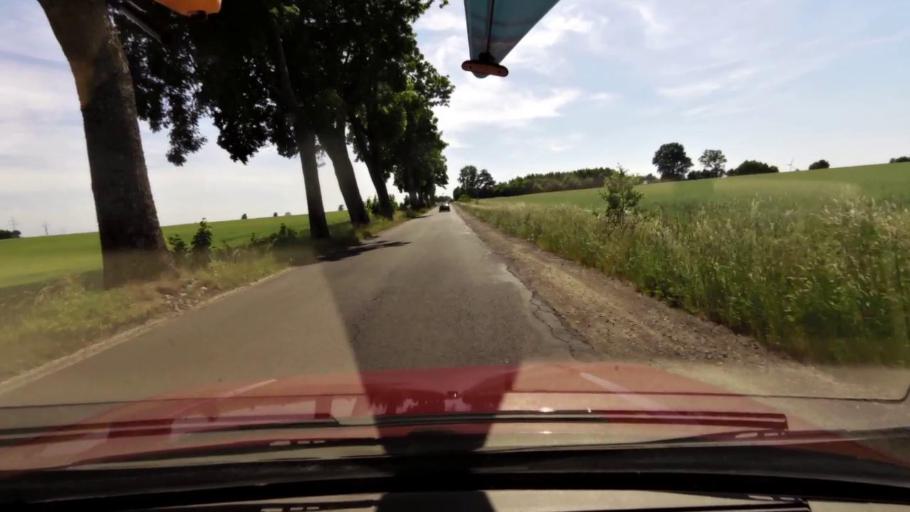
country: PL
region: Pomeranian Voivodeship
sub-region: Powiat slupski
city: Kobylnica
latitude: 54.3994
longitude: 16.9939
